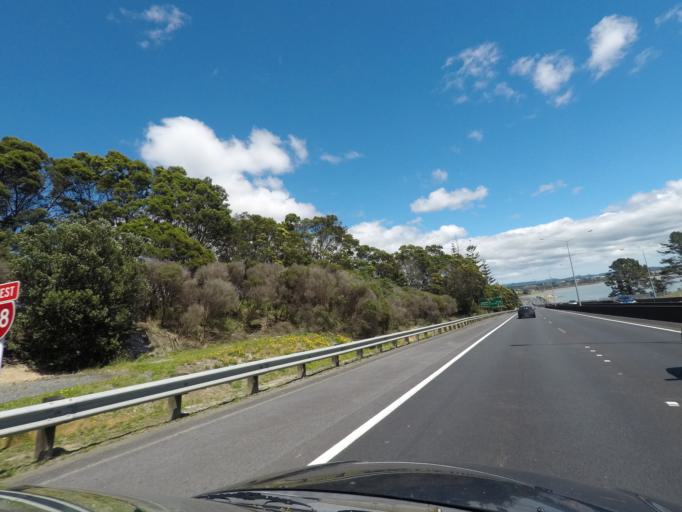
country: NZ
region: Auckland
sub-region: Auckland
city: North Shore
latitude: -36.7839
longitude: 174.6723
